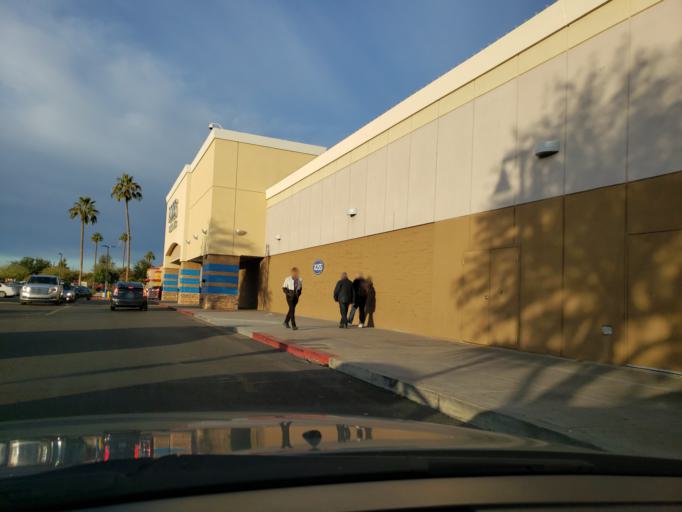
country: US
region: Arizona
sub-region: Maricopa County
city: Phoenix
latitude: 33.5222
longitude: -112.0982
